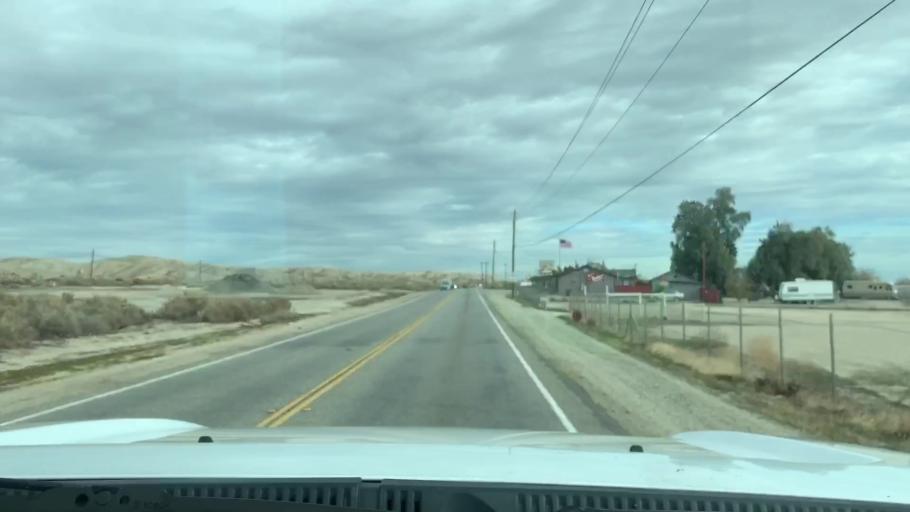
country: US
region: California
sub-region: Kern County
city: Ford City
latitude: 35.2296
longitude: -119.3753
